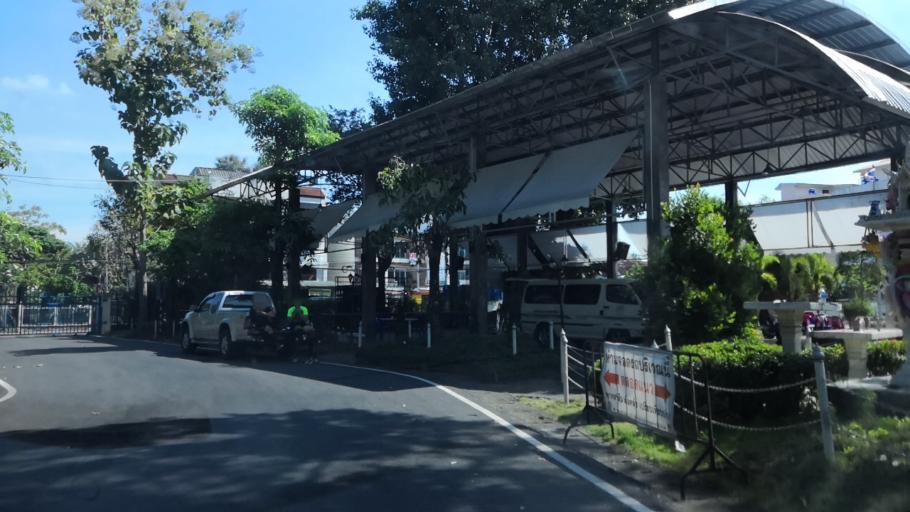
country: TH
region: Chiang Mai
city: Chiang Mai
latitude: 18.8100
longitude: 98.9700
